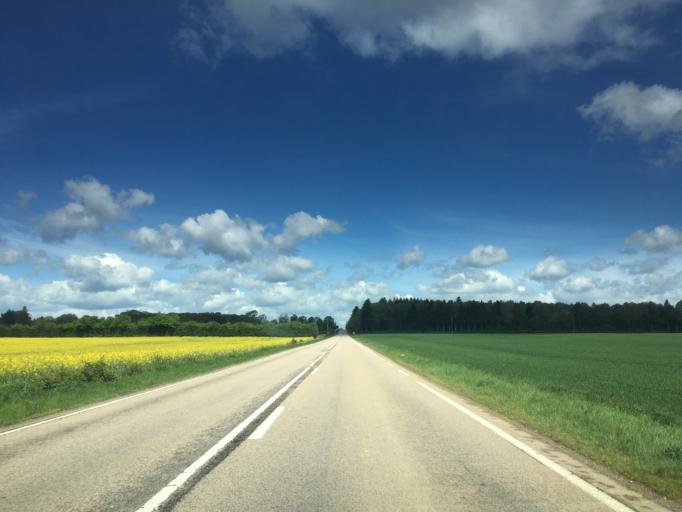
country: FR
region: Lower Normandy
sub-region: Departement de l'Orne
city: Rai
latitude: 48.7770
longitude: 0.6077
